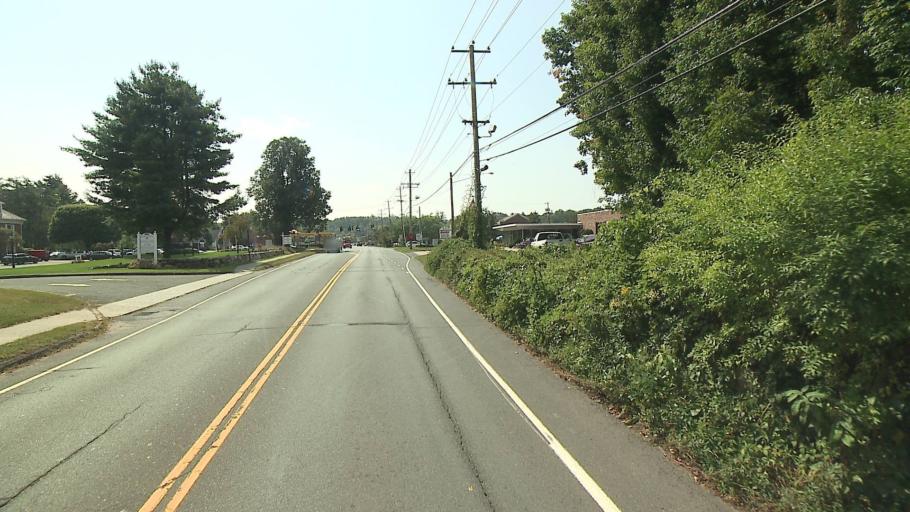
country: US
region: Connecticut
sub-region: Fairfield County
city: Ridgefield
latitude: 41.2962
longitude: -73.4927
